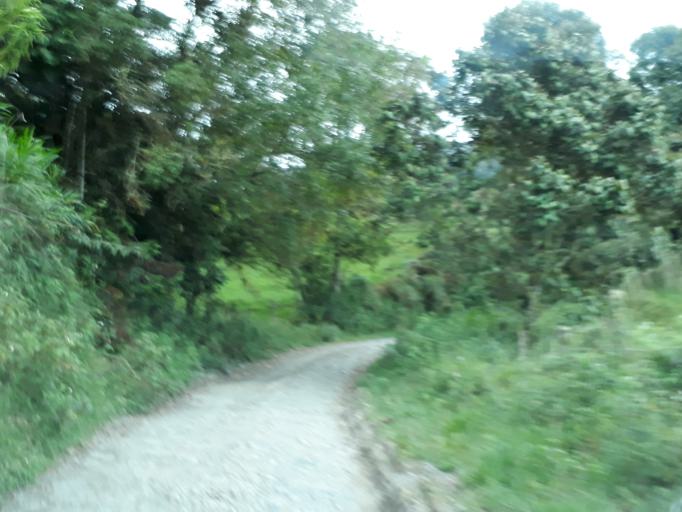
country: CO
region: Boyaca
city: Muzo
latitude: 5.3762
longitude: -74.0725
